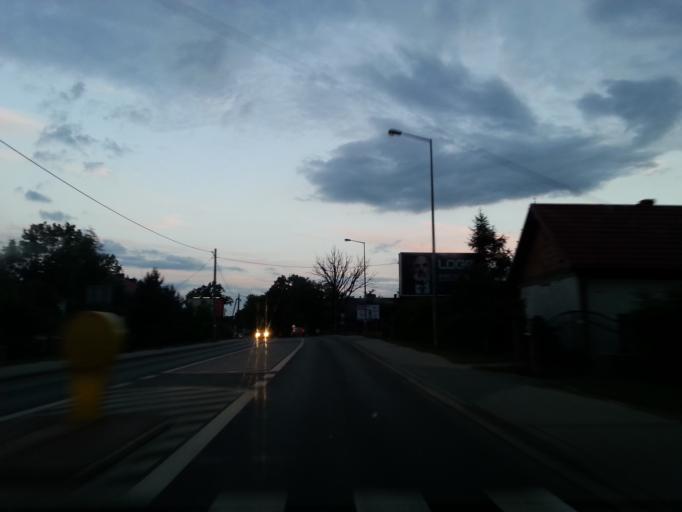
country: PL
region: Lower Silesian Voivodeship
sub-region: Powiat wroclawski
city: Bielany Wroclawskie
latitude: 51.0440
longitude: 16.9700
